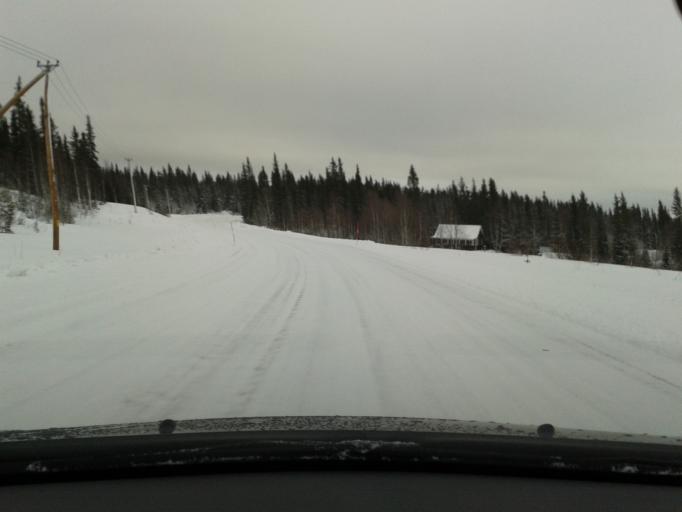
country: SE
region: Vaesterbotten
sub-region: Vilhelmina Kommun
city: Sjoberg
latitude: 65.2249
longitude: 15.9447
